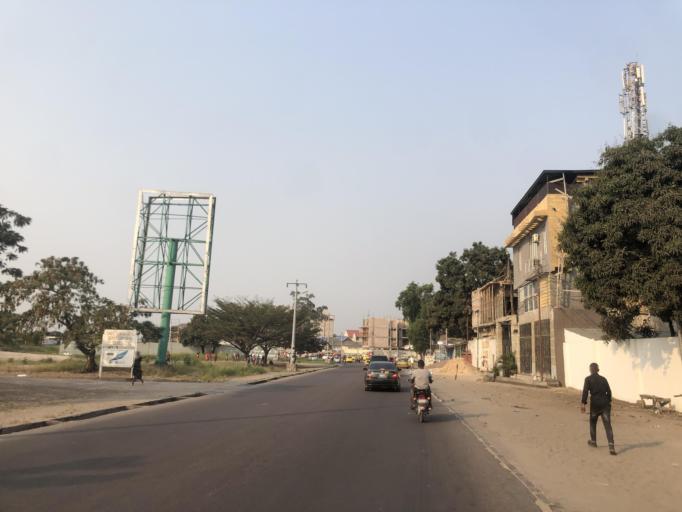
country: CD
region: Kinshasa
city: Kinshasa
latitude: -4.3301
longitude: 15.3285
